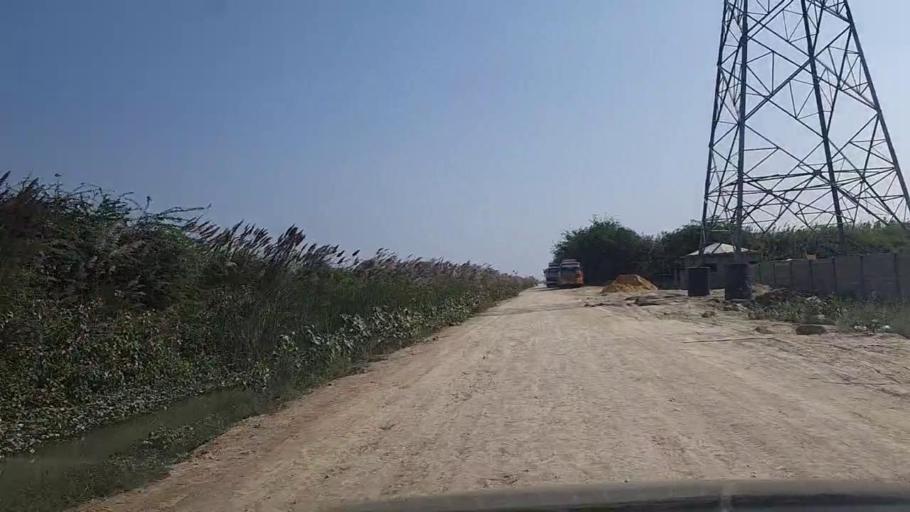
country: PK
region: Sindh
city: Gharo
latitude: 24.7208
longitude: 67.5568
